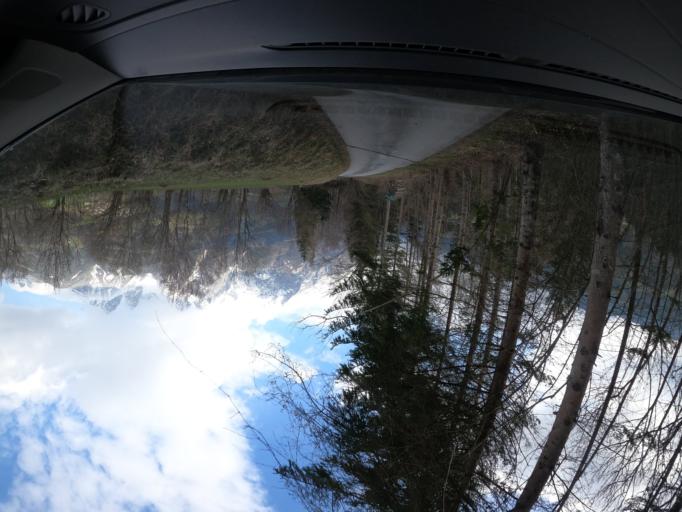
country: AT
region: Salzburg
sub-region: Politischer Bezirk Sankt Johann im Pongau
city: Pfarrwerfen
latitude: 47.4559
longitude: 13.1930
